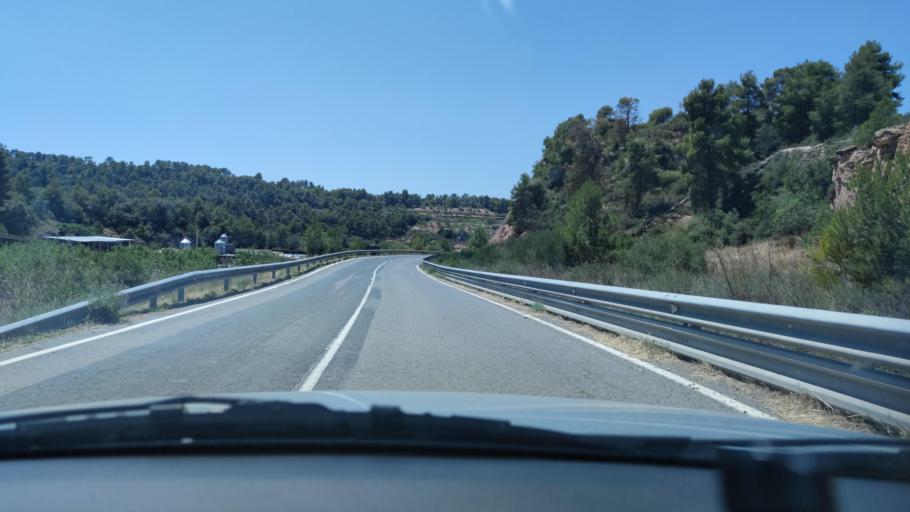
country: ES
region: Catalonia
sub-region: Provincia de Lleida
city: Juncosa
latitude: 41.3769
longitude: 0.7633
